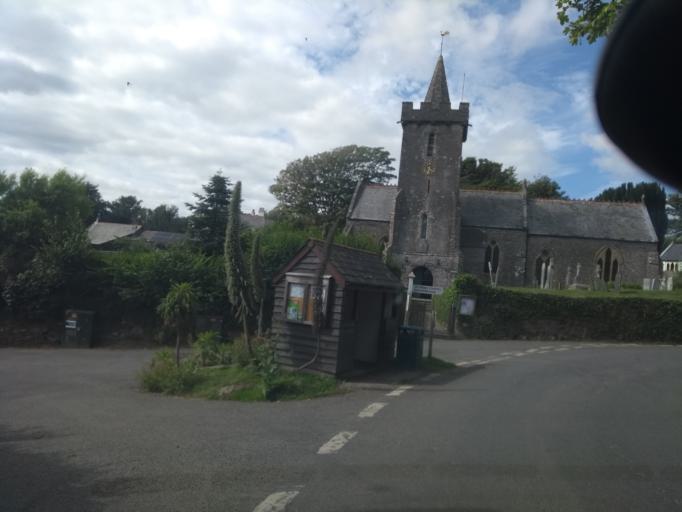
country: GB
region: England
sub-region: Devon
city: Modbury
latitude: 50.2980
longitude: -3.8931
